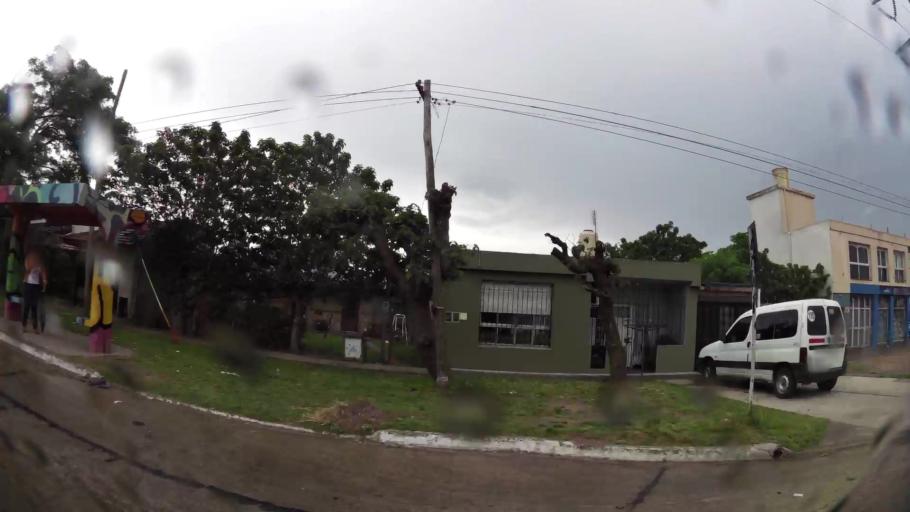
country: AR
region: Buenos Aires
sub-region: Partido de Quilmes
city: Quilmes
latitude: -34.7723
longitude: -58.2302
